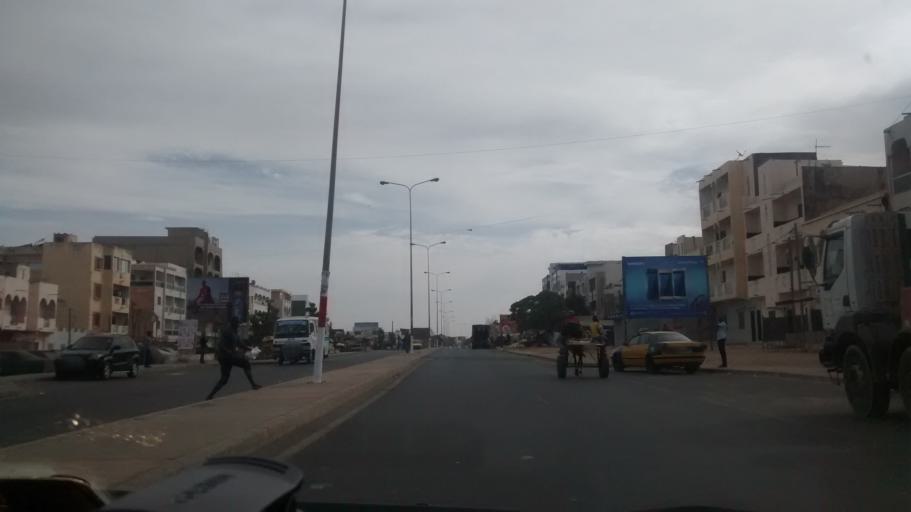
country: SN
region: Dakar
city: Pikine
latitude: 14.7762
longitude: -17.3988
